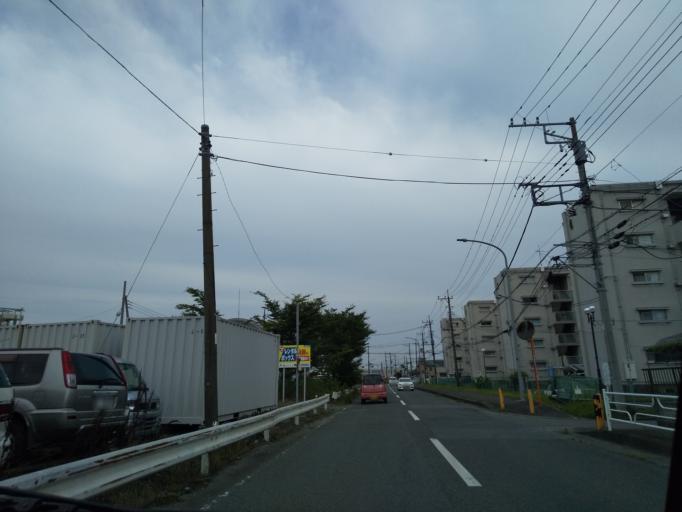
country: JP
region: Kanagawa
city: Atsugi
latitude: 35.4743
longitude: 139.3537
